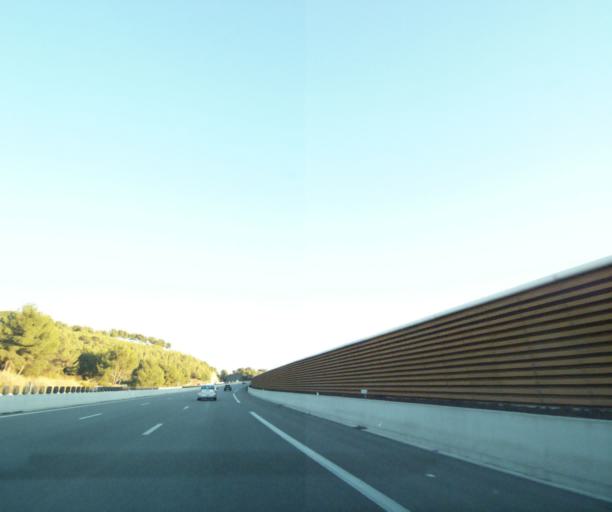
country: FR
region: Provence-Alpes-Cote d'Azur
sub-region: Departement des Bouches-du-Rhone
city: Ceyreste
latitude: 43.1949
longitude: 5.6484
